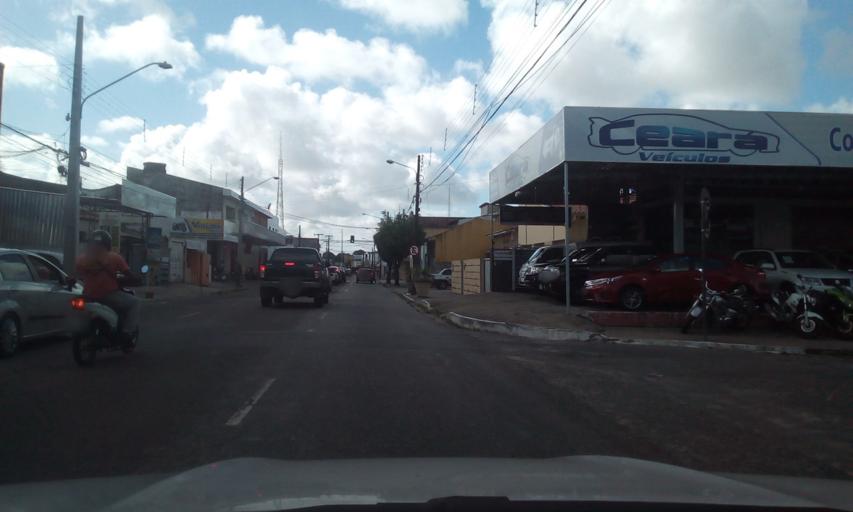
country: BR
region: Paraiba
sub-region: Joao Pessoa
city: Joao Pessoa
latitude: -7.1311
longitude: -34.8788
